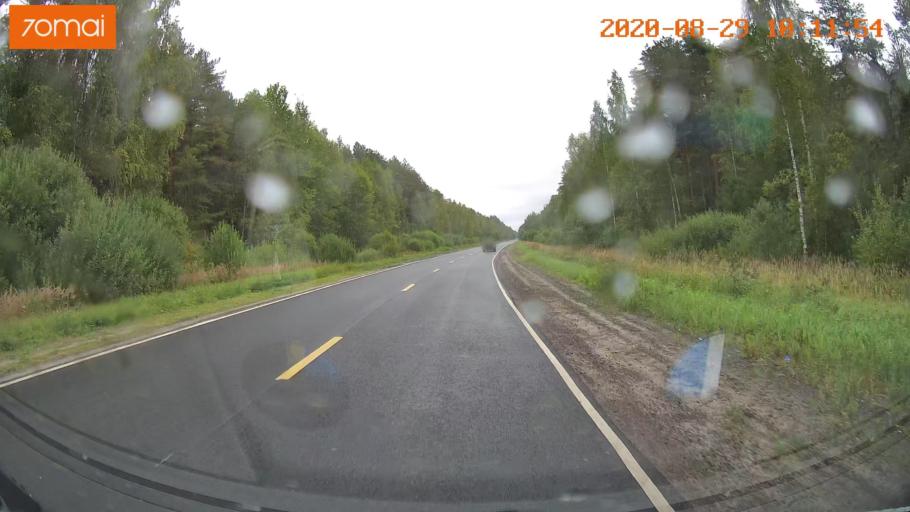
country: RU
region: Ivanovo
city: Kuznechikha
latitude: 57.3741
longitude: 42.6959
